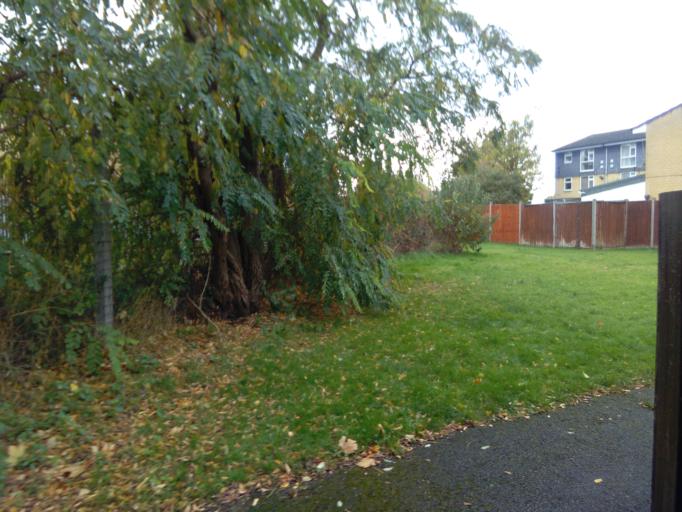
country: GB
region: England
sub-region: Greater London
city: Feltham
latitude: 51.4470
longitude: -0.4151
